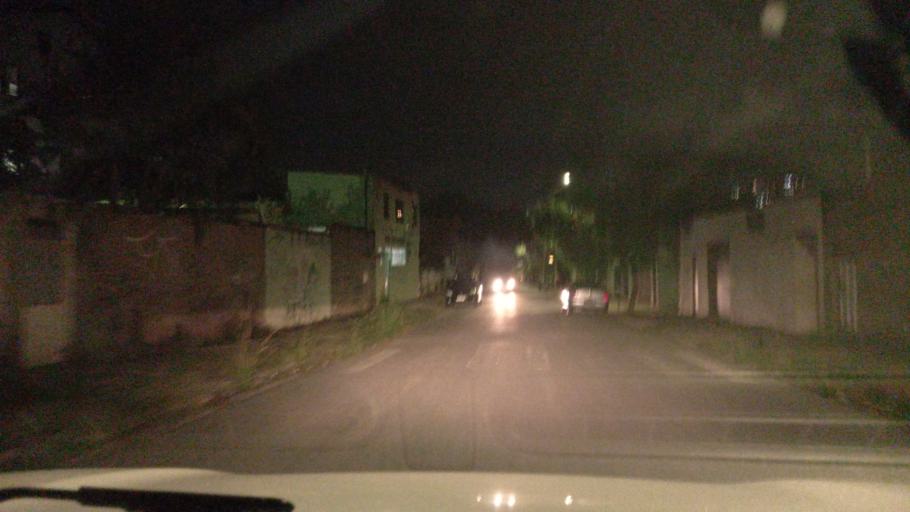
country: BR
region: Minas Gerais
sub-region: Belo Horizonte
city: Belo Horizonte
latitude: -19.8798
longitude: -43.9382
